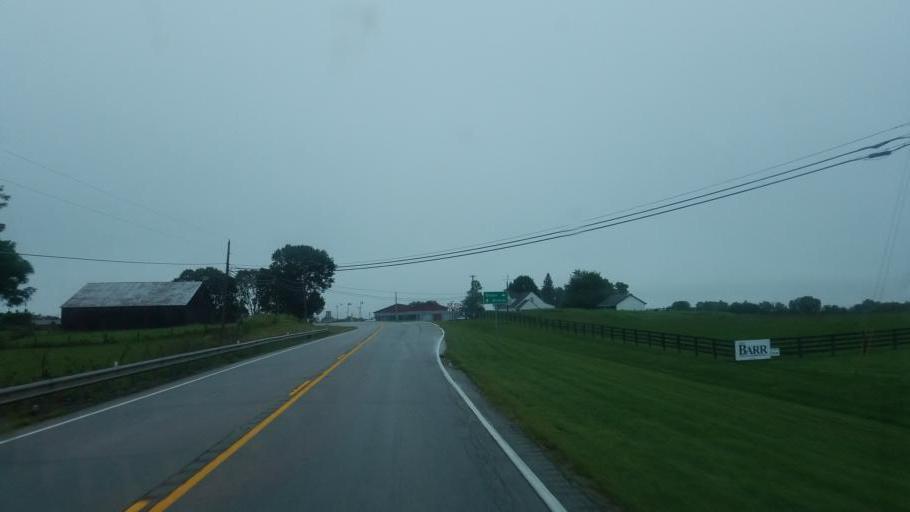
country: US
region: Kentucky
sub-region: Fleming County
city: Flemingsburg
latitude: 38.3942
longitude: -83.6933
